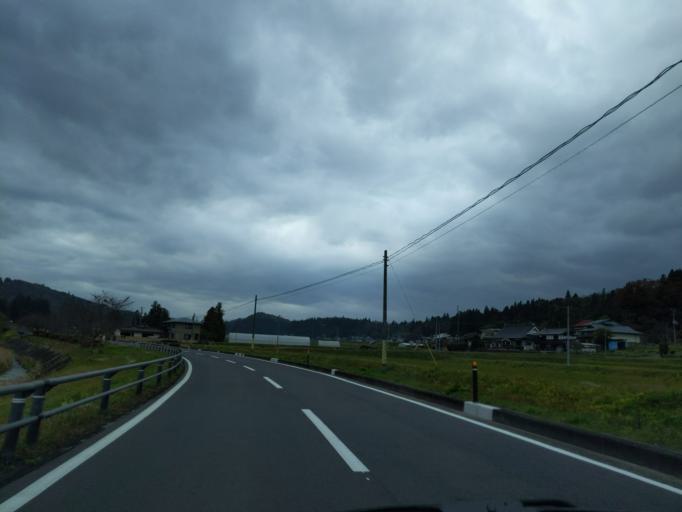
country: JP
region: Iwate
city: Ichinoseki
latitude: 38.9763
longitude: 141.0891
